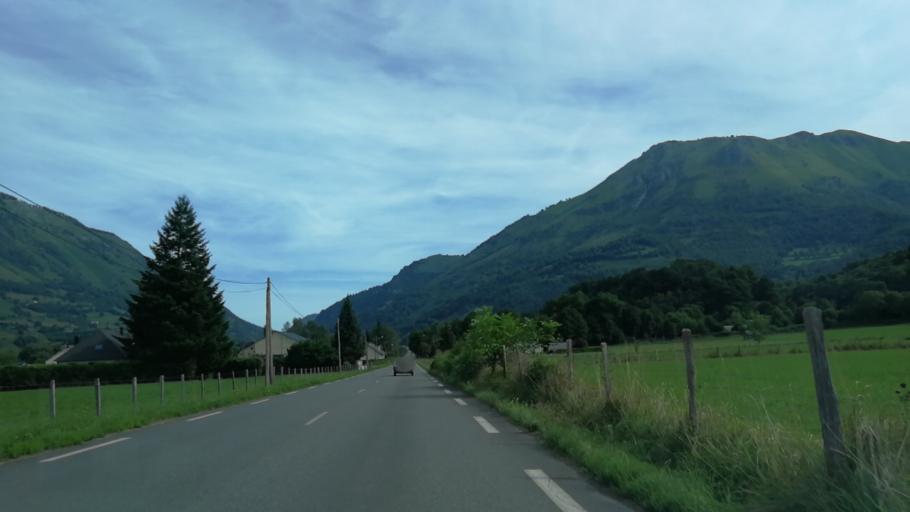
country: FR
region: Aquitaine
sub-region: Departement des Pyrenees-Atlantiques
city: Arette
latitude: 42.9819
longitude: -0.6053
